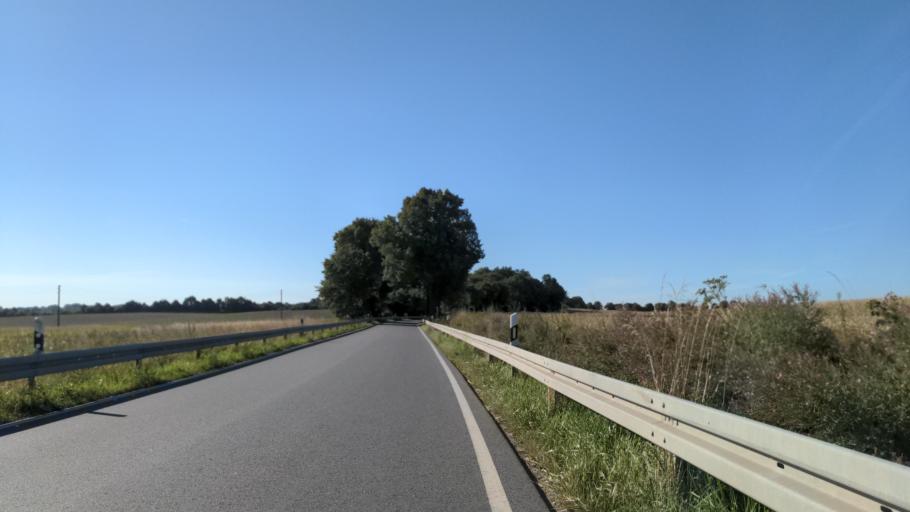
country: DE
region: Mecklenburg-Vorpommern
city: Dassow
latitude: 53.8979
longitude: 10.9574
